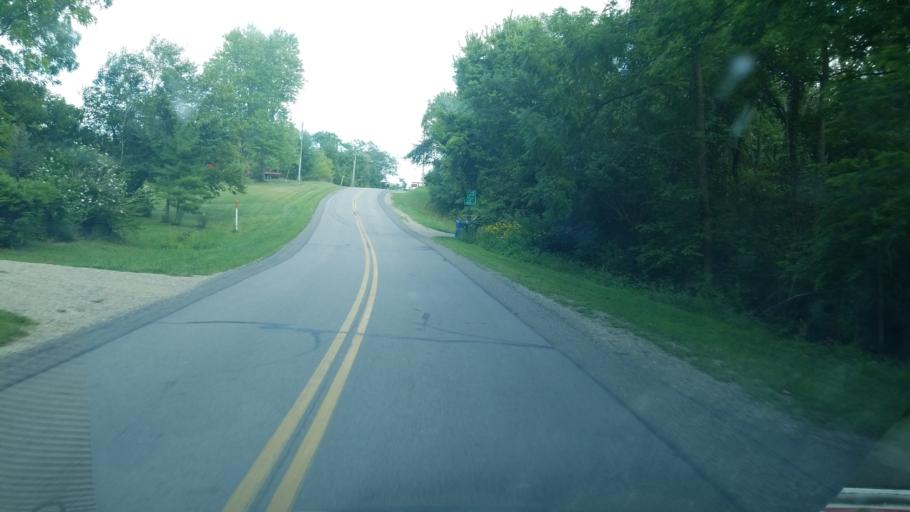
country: US
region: Ohio
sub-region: Champaign County
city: Saint Paris
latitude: 40.1576
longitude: -83.9103
